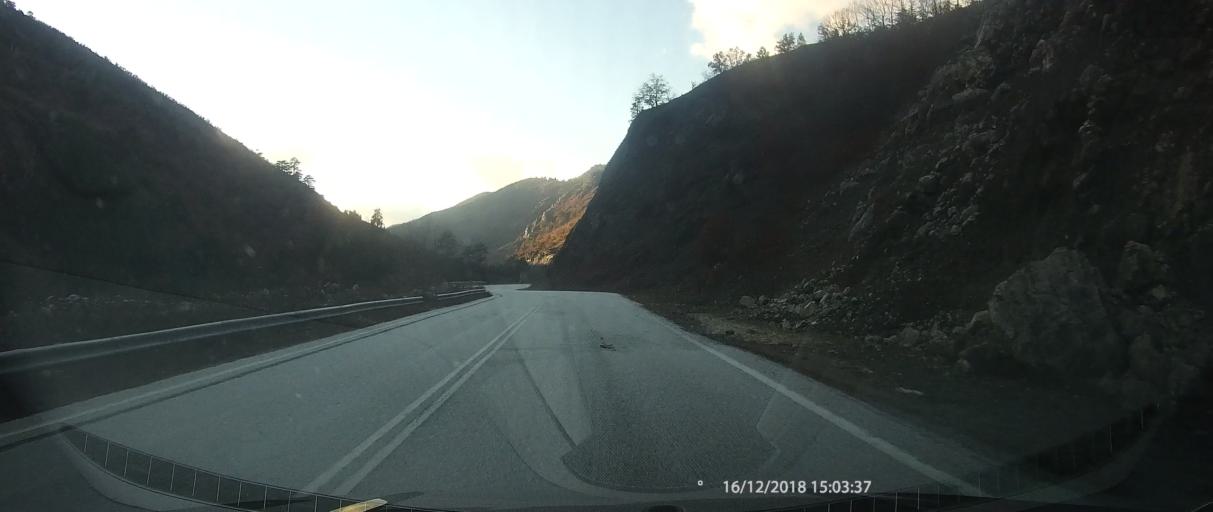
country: GR
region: West Macedonia
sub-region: Nomos Kastorias
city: Nestorio
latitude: 40.2278
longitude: 20.9799
